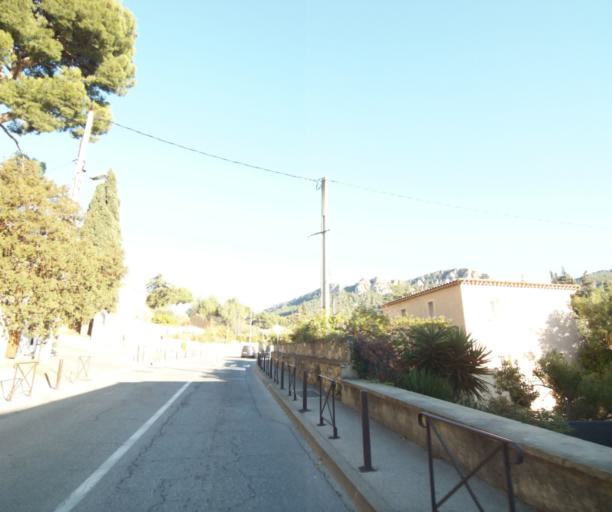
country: FR
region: Provence-Alpes-Cote d'Azur
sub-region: Departement des Bouches-du-Rhone
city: Cassis
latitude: 43.2155
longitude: 5.5451
